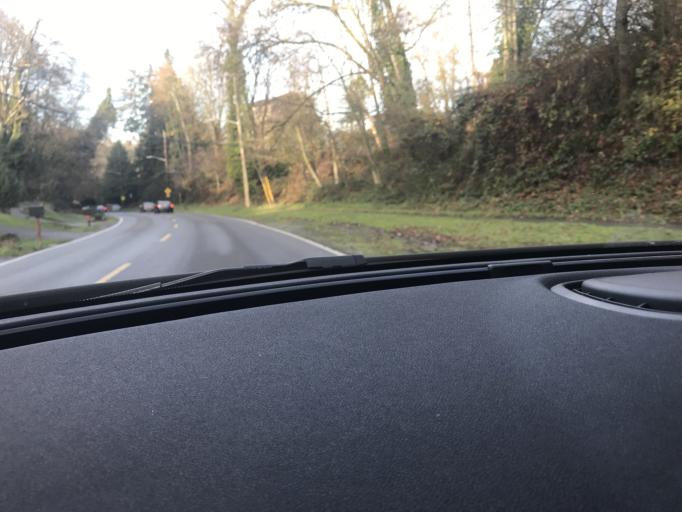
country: US
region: Washington
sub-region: King County
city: White Center
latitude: 47.5361
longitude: -122.3576
